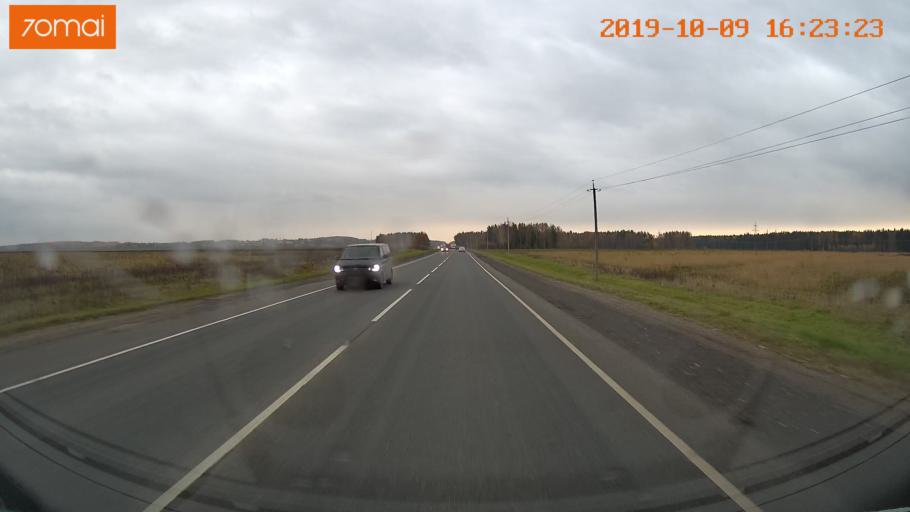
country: RU
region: Kostroma
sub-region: Kostromskoy Rayon
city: Kostroma
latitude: 57.6647
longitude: 40.8985
